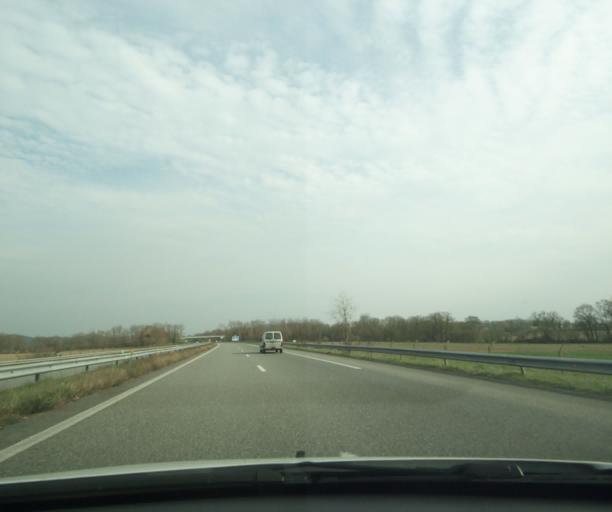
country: FR
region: Aquitaine
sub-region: Departement des Pyrenees-Atlantiques
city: Mont
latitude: 43.4255
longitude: -0.6183
